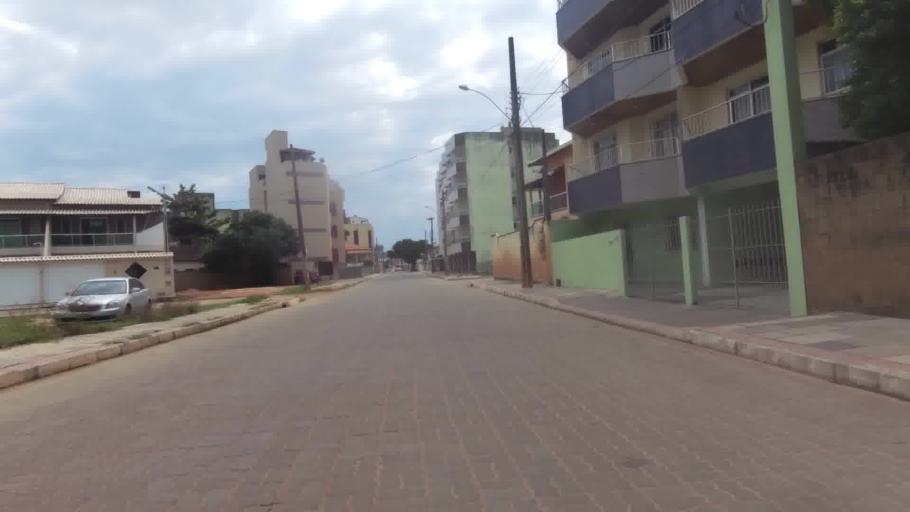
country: BR
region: Espirito Santo
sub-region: Piuma
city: Piuma
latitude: -20.8455
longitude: -40.7438
